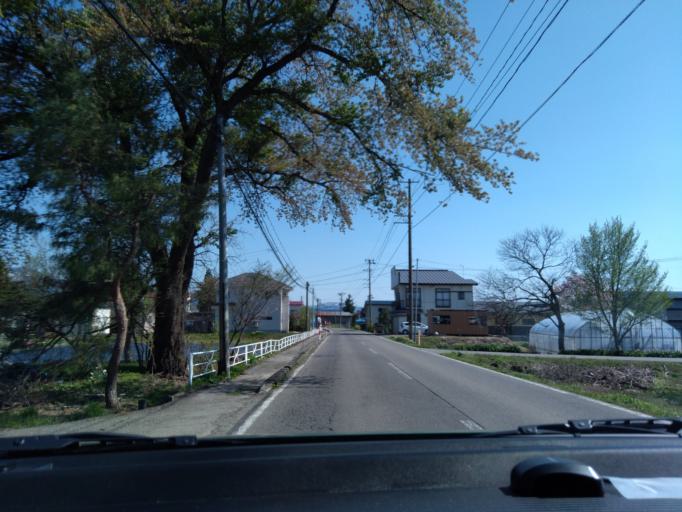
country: JP
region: Akita
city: Kakunodatemachi
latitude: 39.5186
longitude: 140.5891
